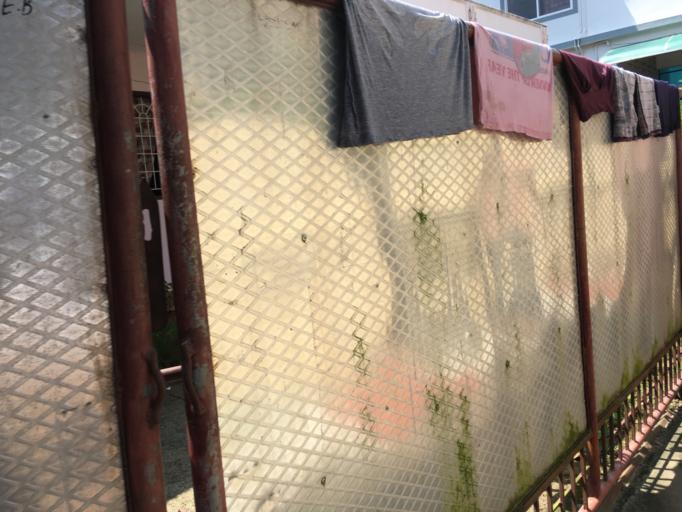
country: IN
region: Kerala
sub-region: Ernakulam
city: Cochin
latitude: 9.9595
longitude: 76.2447
